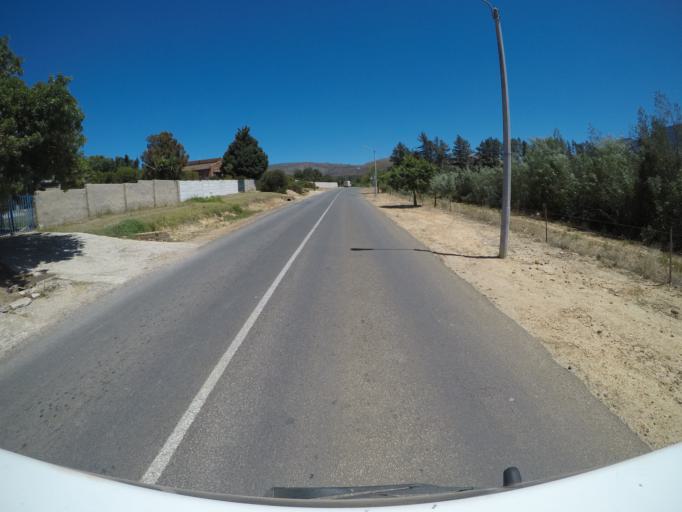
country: ZA
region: Western Cape
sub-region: Overberg District Municipality
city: Hermanus
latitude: -34.2236
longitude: 19.2015
